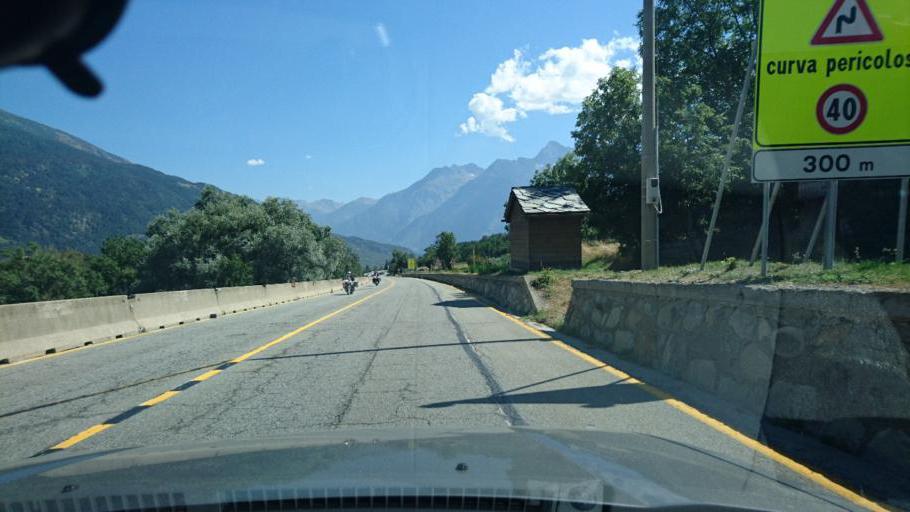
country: IT
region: Aosta Valley
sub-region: Valle d'Aosta
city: Allein
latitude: 45.7953
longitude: 7.2843
